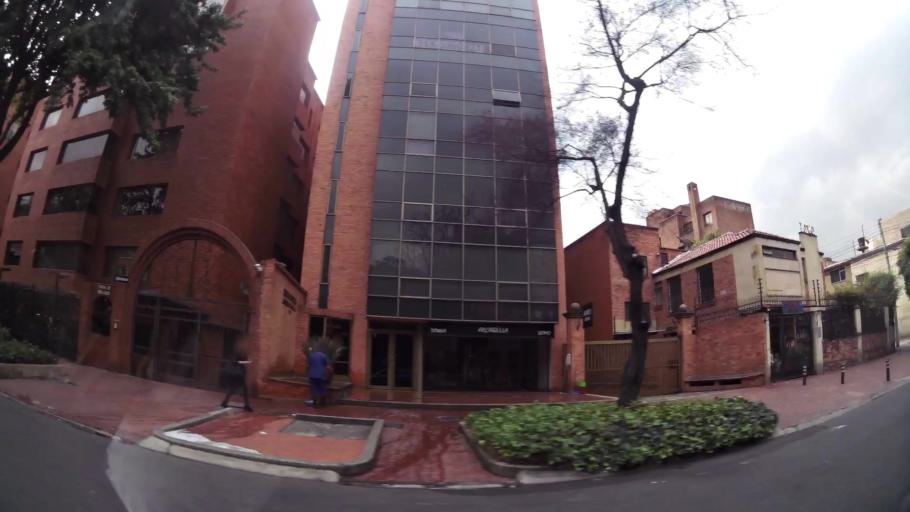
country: CO
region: Bogota D.C.
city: Barrio San Luis
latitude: 4.6646
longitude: -74.0512
